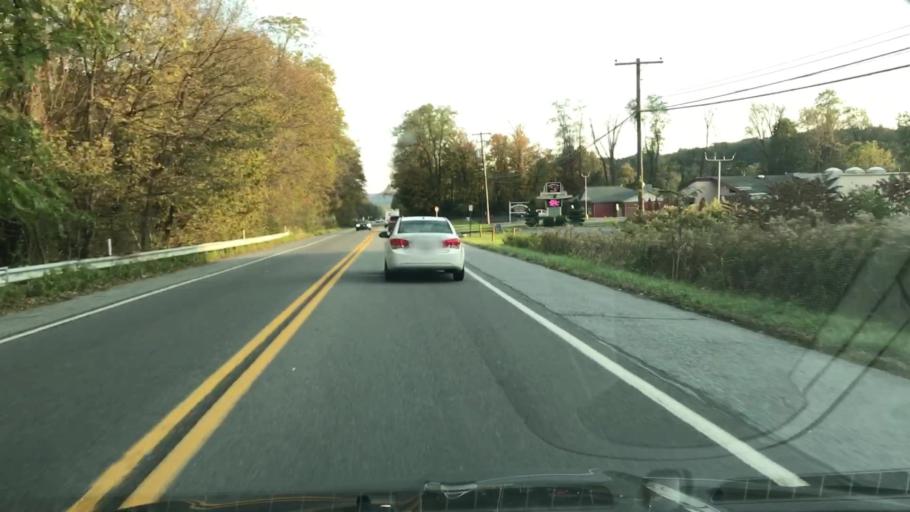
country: US
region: Pennsylvania
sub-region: Dauphin County
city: Bressler
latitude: 40.2357
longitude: -76.8031
